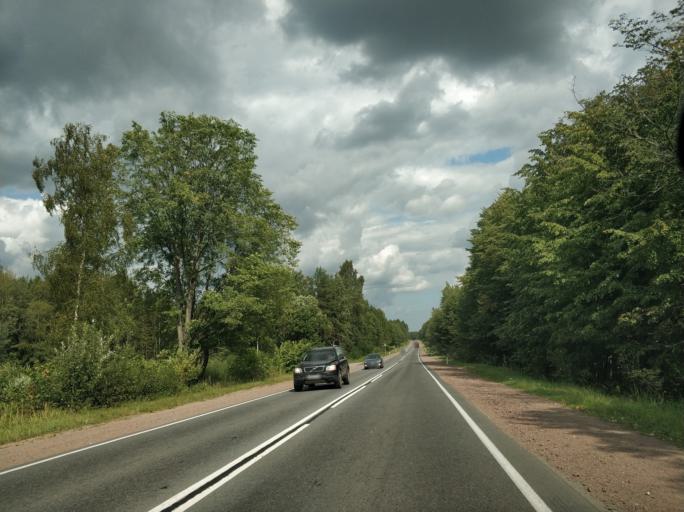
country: RU
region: Leningrad
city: Romanovka
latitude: 60.0717
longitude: 30.7451
